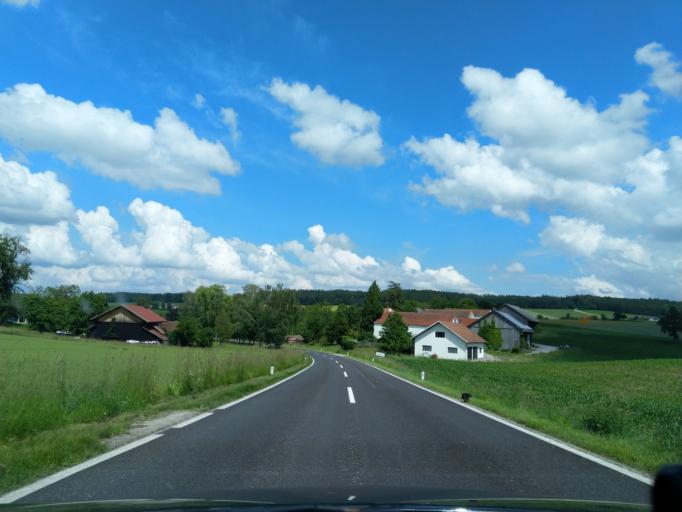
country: DE
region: Bavaria
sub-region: Lower Bavaria
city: Bad Fussing
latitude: 48.2475
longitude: 13.3653
